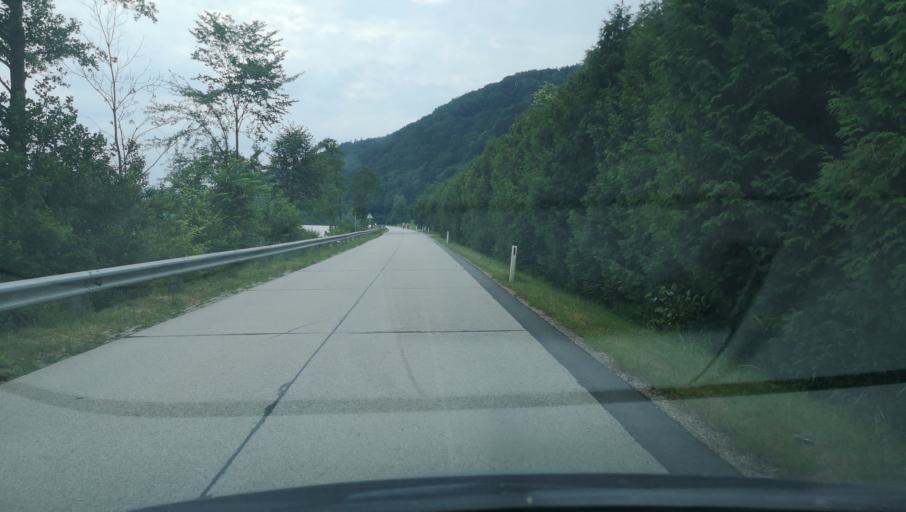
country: AT
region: Lower Austria
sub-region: Politischer Bezirk Melk
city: Nochling
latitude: 48.1915
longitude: 15.0124
